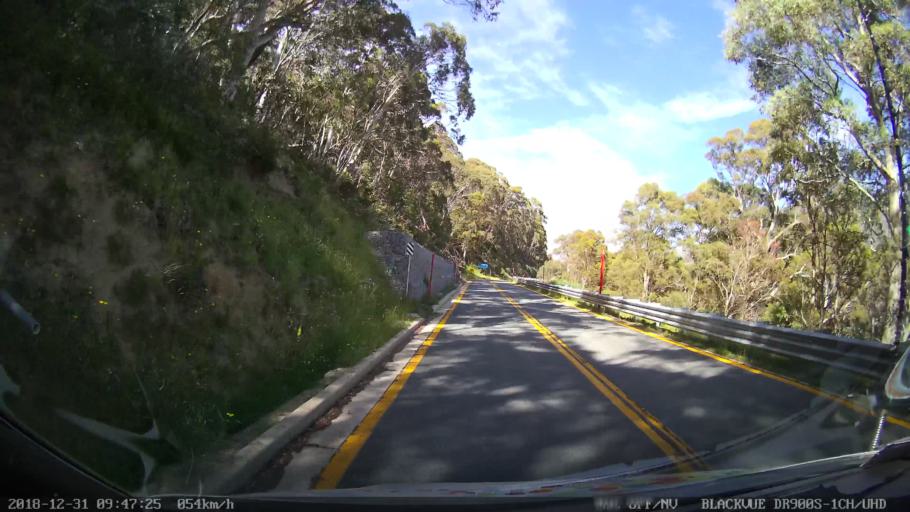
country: AU
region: New South Wales
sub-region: Snowy River
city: Jindabyne
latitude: -36.5083
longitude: 148.3018
